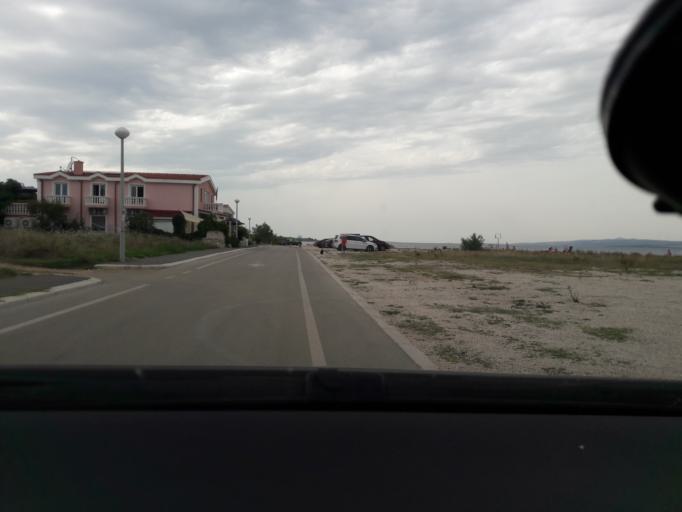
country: HR
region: Zadarska
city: Vir
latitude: 44.3089
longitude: 15.0876
